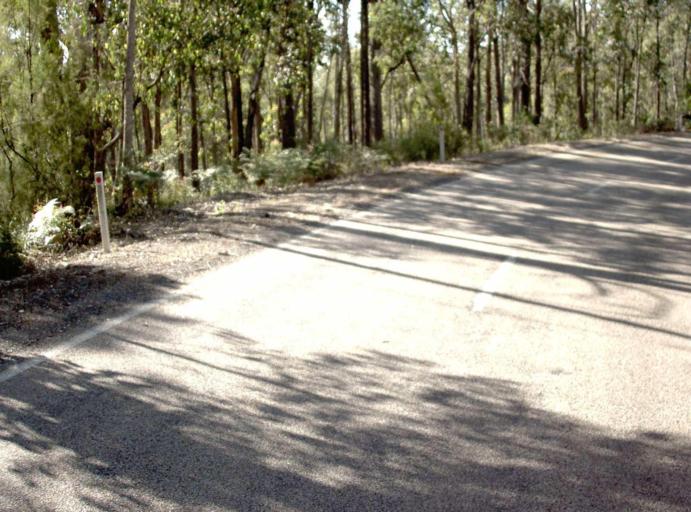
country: AU
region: Victoria
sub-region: East Gippsland
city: Lakes Entrance
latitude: -37.5640
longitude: 148.5590
